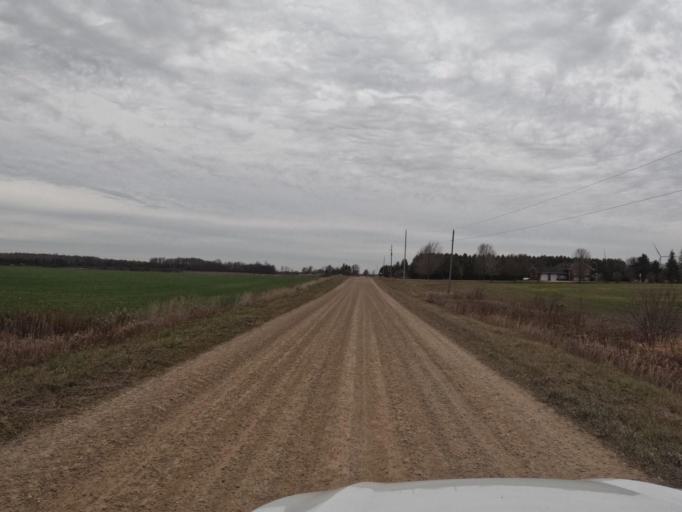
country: CA
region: Ontario
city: Shelburne
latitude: 44.0199
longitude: -80.3690
